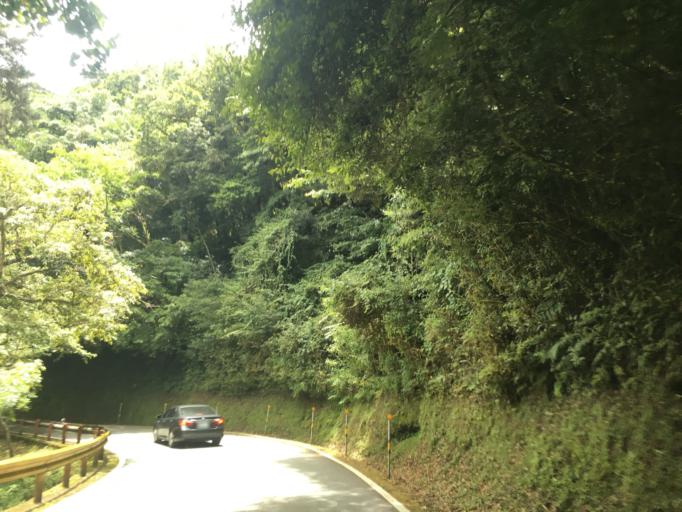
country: TW
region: Taiwan
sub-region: Hualien
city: Hualian
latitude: 24.1803
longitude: 121.3955
